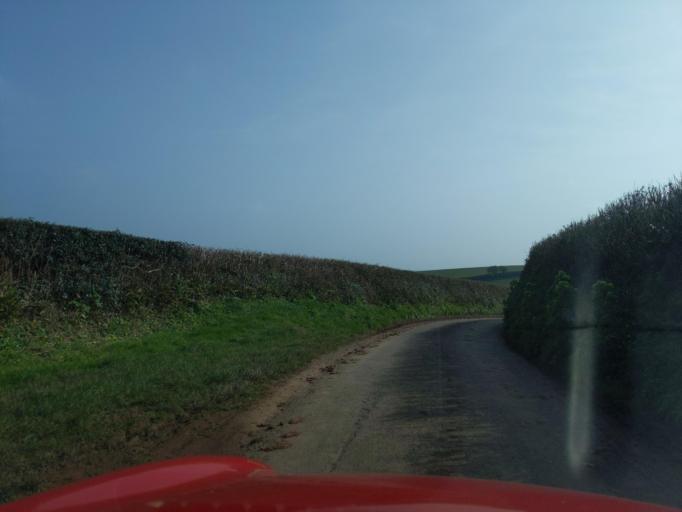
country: GB
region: England
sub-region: Devon
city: Kingsbridge
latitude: 50.2878
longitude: -3.7337
